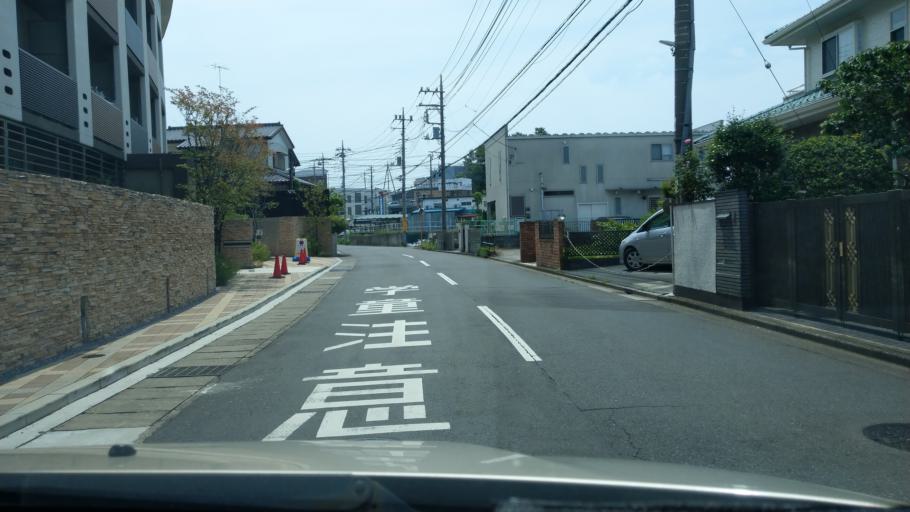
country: JP
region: Saitama
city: Saitama
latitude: 35.9092
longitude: 139.6498
